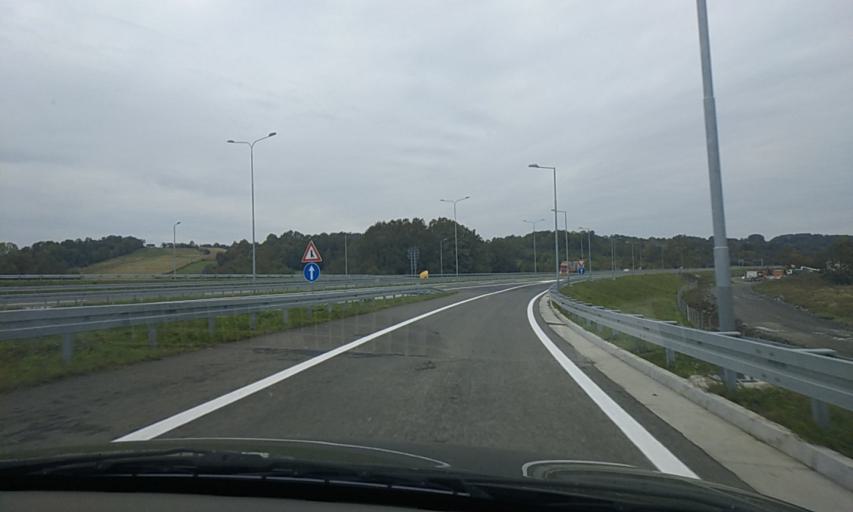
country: BA
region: Republika Srpska
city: Prnjavor
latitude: 44.8487
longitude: 17.6752
